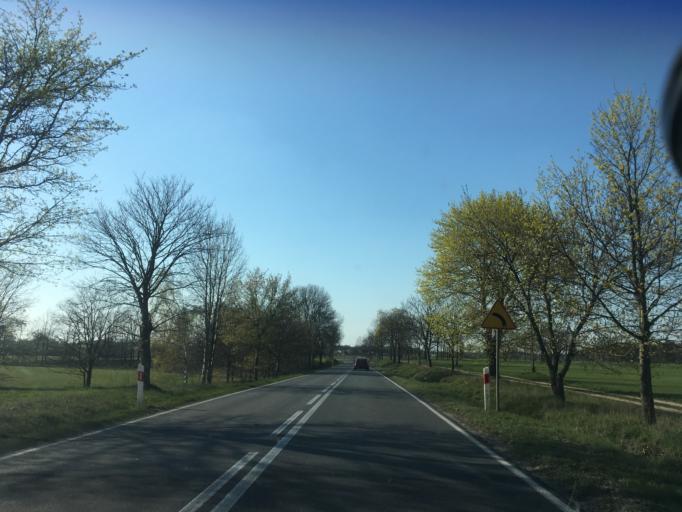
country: PL
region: Lubusz
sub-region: Powiat zaganski
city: Szprotawa
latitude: 51.5064
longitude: 15.6192
